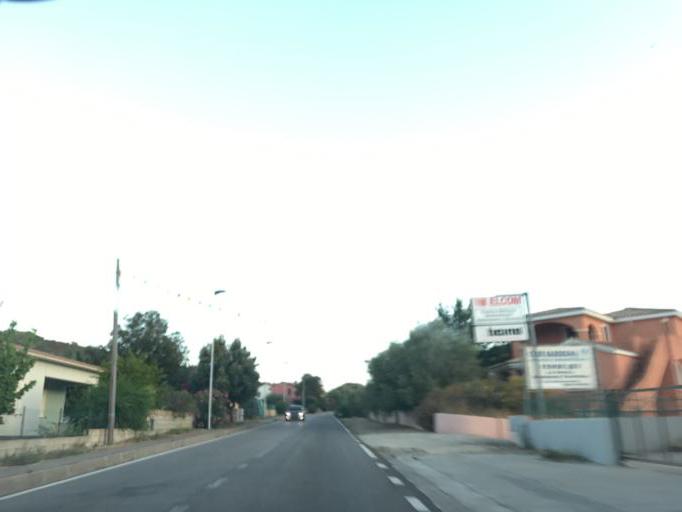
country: IT
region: Sardinia
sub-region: Provincia di Olbia-Tempio
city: San Teodoro
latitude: 40.7468
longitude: 9.6470
